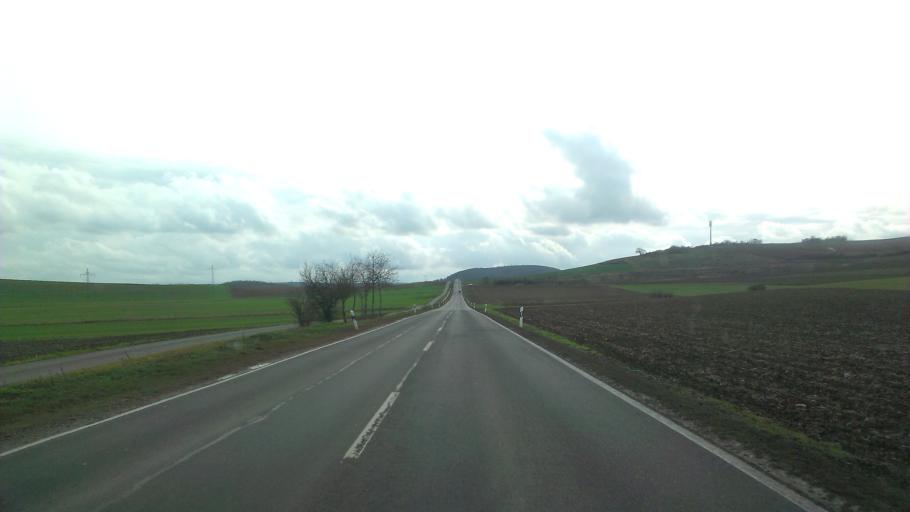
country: DE
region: Rheinland-Pfalz
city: Hackenheim
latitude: 49.8180
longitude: 7.9065
